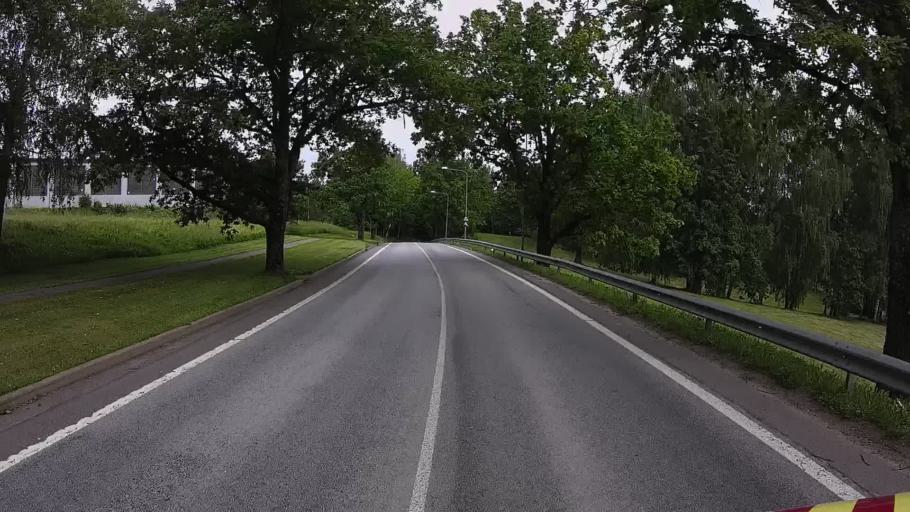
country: EE
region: Viljandimaa
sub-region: Karksi vald
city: Karksi-Nuia
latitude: 58.1064
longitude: 25.5472
